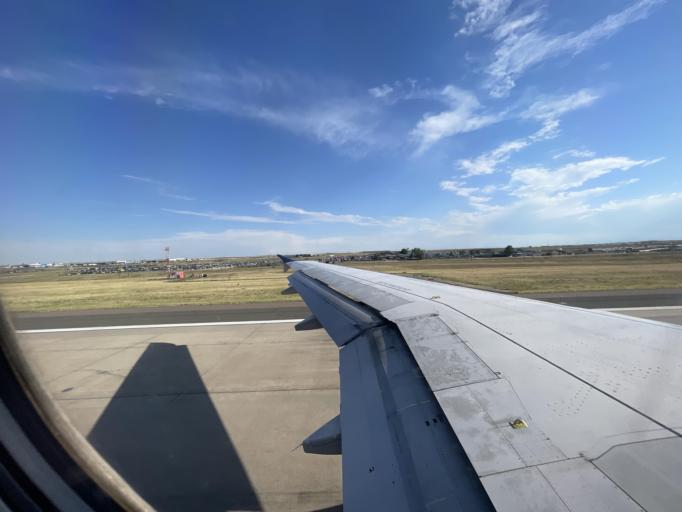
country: US
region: Colorado
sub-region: Weld County
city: Lochbuie
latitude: 39.8407
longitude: -104.6885
